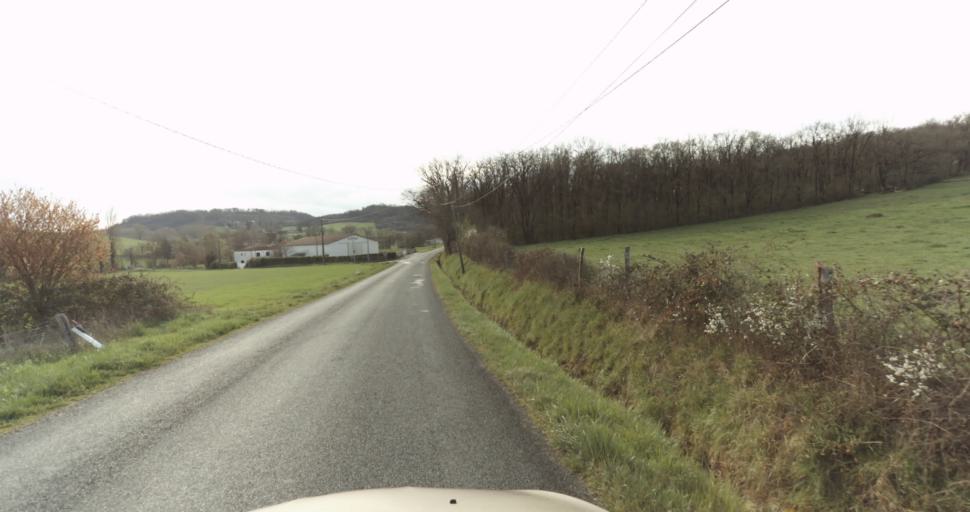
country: FR
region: Midi-Pyrenees
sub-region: Departement du Tarn
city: Puygouzon
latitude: 43.9071
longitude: 2.1815
